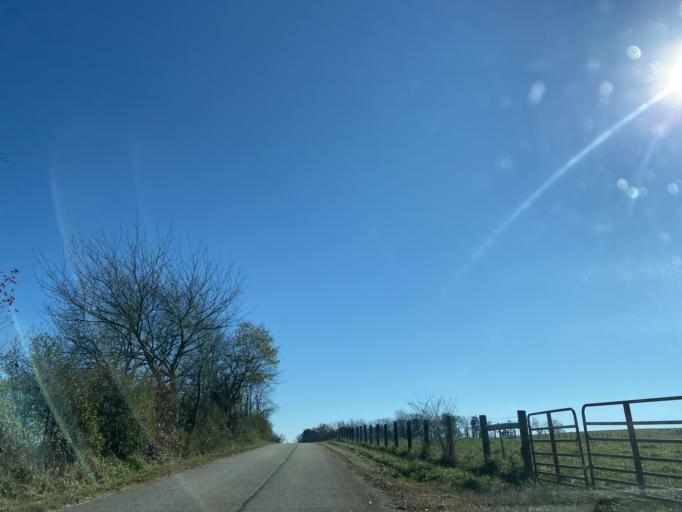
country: US
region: South Carolina
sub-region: Spartanburg County
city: Mayo
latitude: 35.1392
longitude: -81.7702
